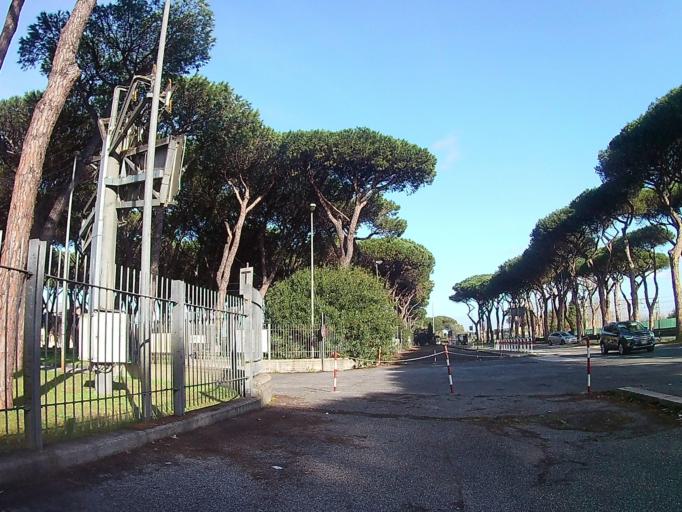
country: IT
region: Latium
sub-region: Citta metropolitana di Roma Capitale
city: Lido di Ostia
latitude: 41.7459
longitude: 12.2879
